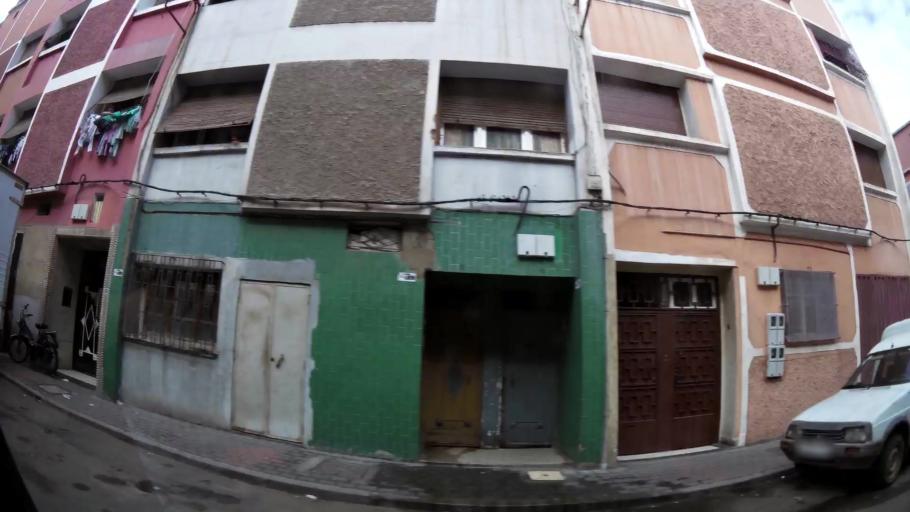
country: MA
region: Grand Casablanca
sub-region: Casablanca
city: Casablanca
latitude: 33.5843
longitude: -7.5740
